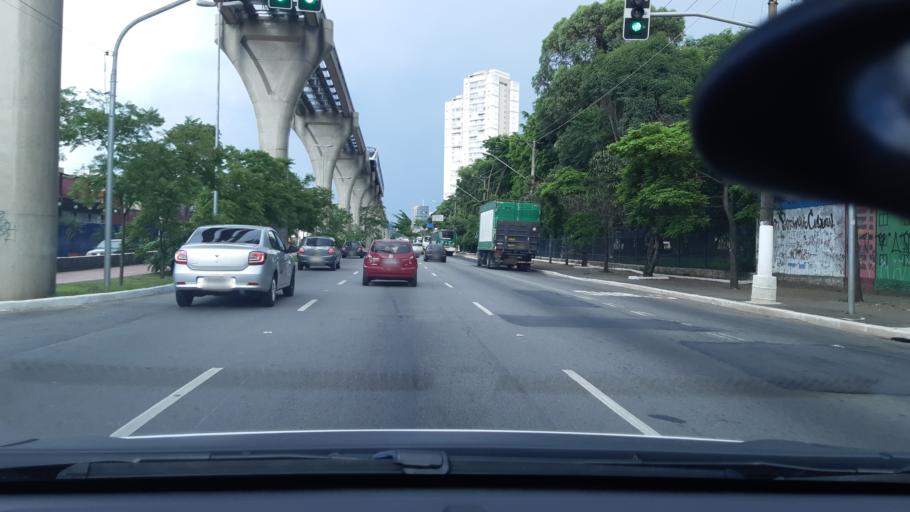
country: BR
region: Sao Paulo
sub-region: Sao Caetano Do Sul
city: Sao Caetano do Sul
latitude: -23.5829
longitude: -46.5676
